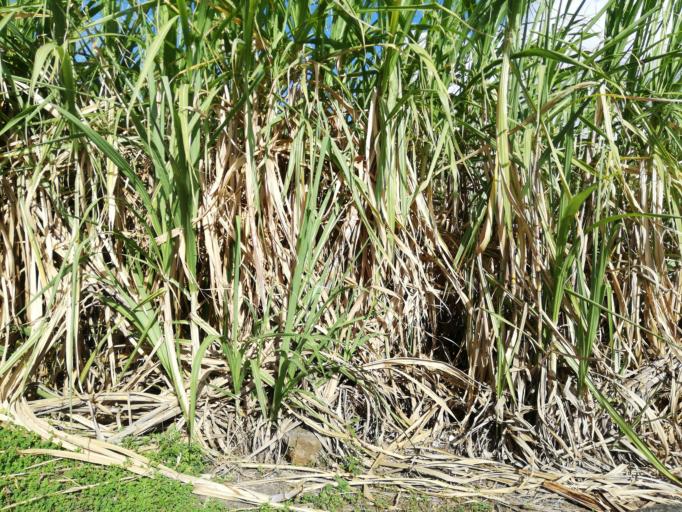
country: MU
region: Riviere du Rempart
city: Grand Baie
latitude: -20.0207
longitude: 57.5830
